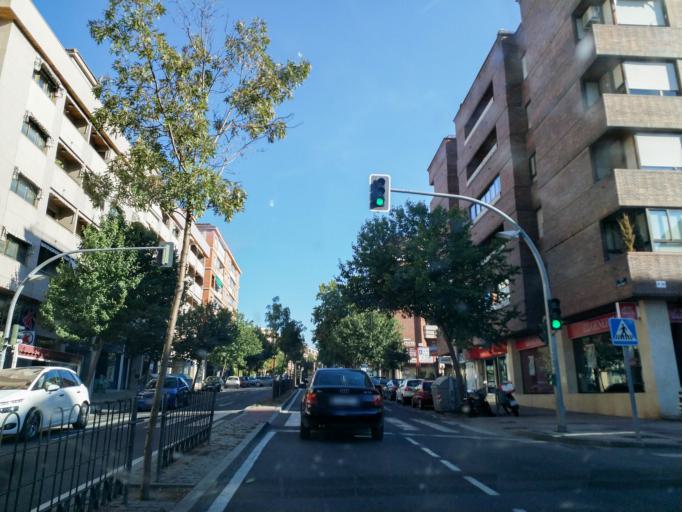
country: ES
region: Castille and Leon
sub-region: Provincia de Segovia
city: Segovia
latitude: 40.9435
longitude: -4.1200
